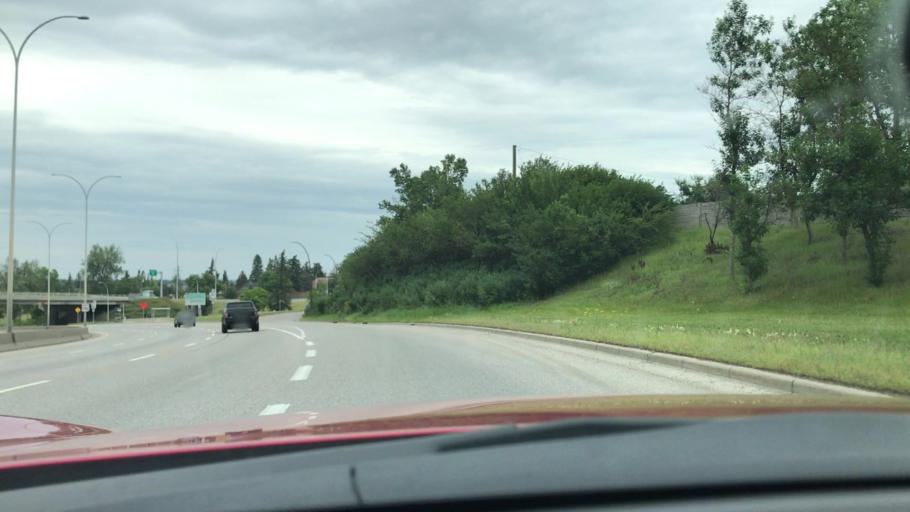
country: CA
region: Alberta
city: Calgary
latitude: 51.0363
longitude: -114.1146
